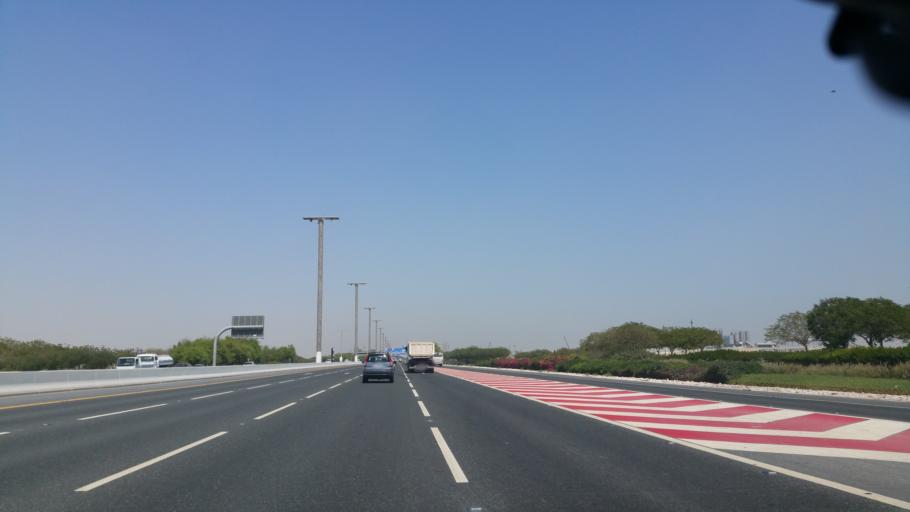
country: QA
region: Al Wakrah
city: Al Wakrah
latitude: 25.2443
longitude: 51.5898
